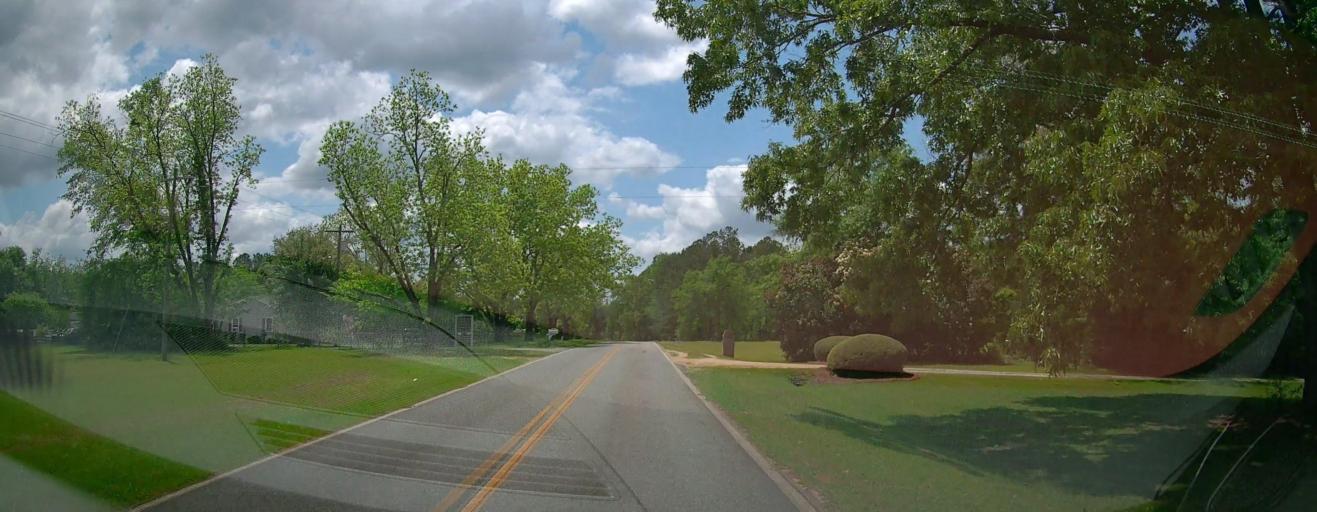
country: US
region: Georgia
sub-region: Laurens County
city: Dublin
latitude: 32.6255
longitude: -82.9884
